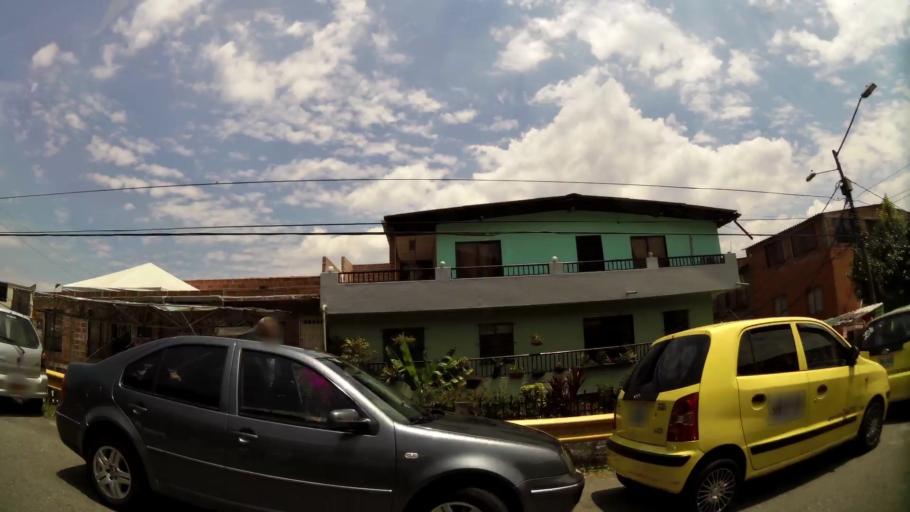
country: CO
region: Antioquia
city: Bello
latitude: 6.3007
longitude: -75.5784
